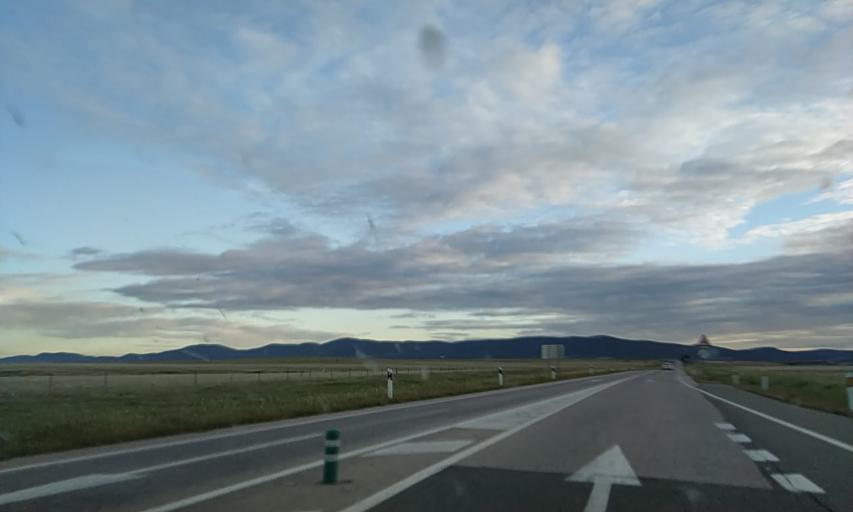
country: ES
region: Extremadura
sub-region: Provincia de Caceres
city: Malpartida de Caceres
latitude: 39.3607
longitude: -6.4634
